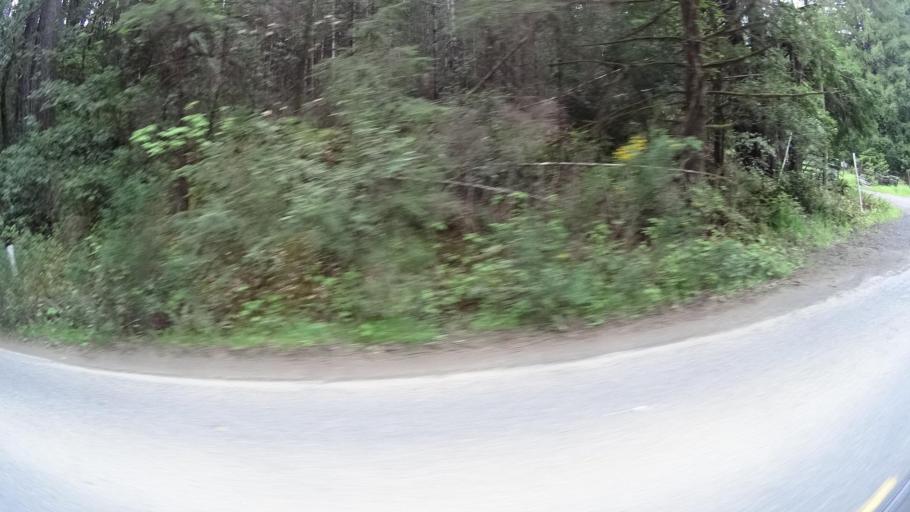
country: US
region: California
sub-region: Humboldt County
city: Redway
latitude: 40.1264
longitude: -123.8455
